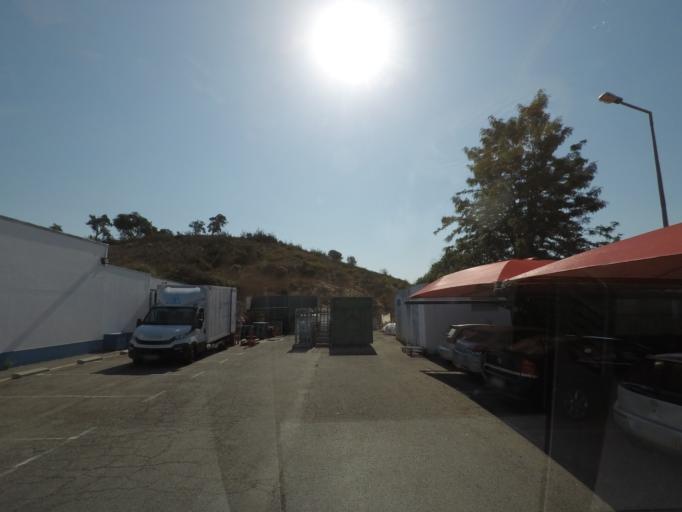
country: PT
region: Beja
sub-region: Odemira
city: Odemira
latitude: 37.5994
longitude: -8.6309
